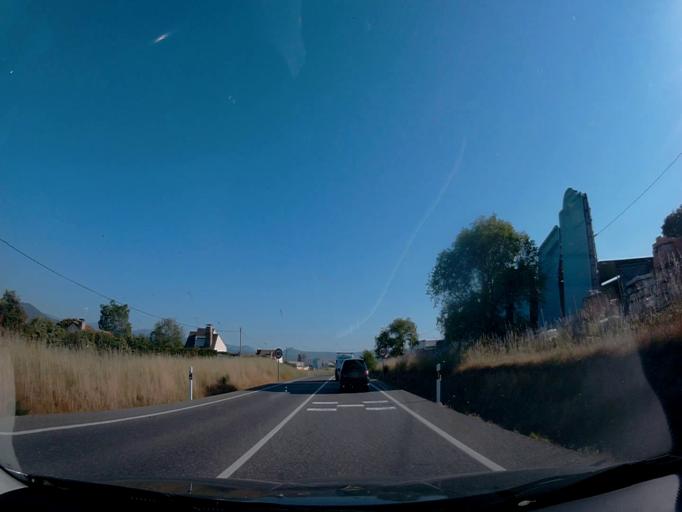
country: ES
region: Castille-La Mancha
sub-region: Province of Toledo
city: Escalona
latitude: 40.1306
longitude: -4.4050
